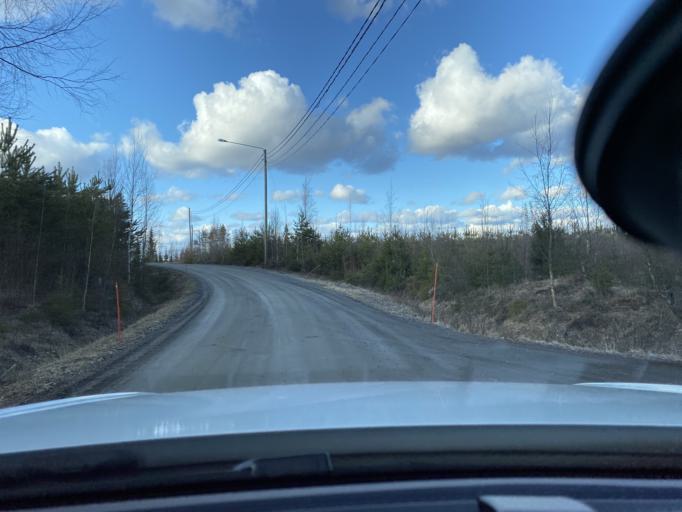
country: FI
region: Pirkanmaa
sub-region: Lounais-Pirkanmaa
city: Punkalaidun
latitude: 61.0937
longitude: 23.1362
